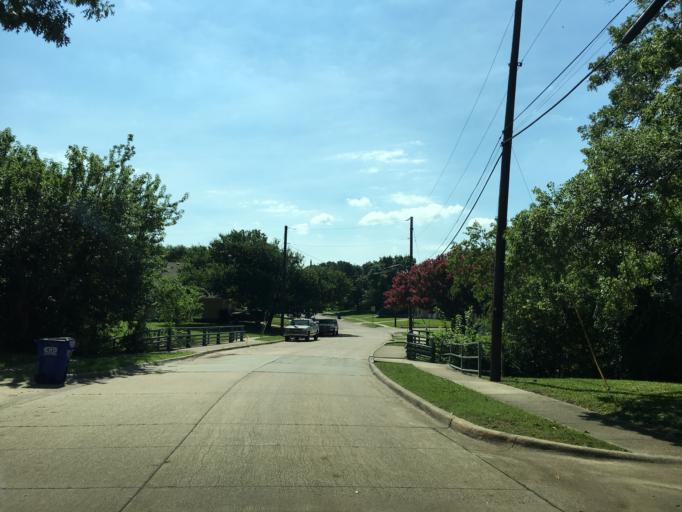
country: US
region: Texas
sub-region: Dallas County
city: Farmers Branch
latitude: 32.9175
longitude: -96.8784
